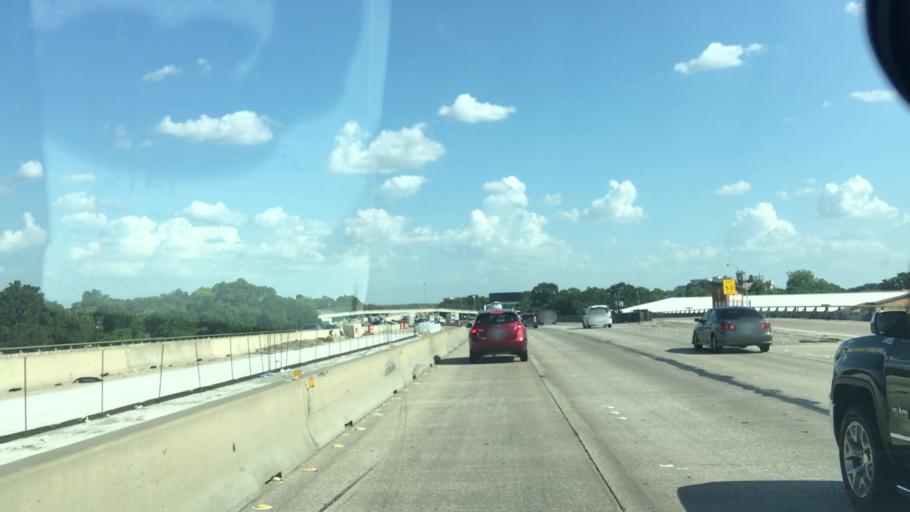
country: US
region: Texas
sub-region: Dallas County
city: Dallas
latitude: 32.7618
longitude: -96.7749
